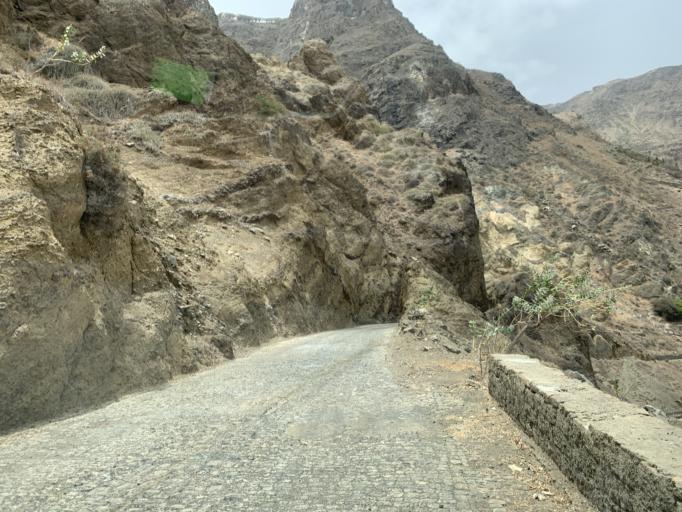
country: CV
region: Brava
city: Vila Nova Sintra
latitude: 14.8752
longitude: -24.7324
